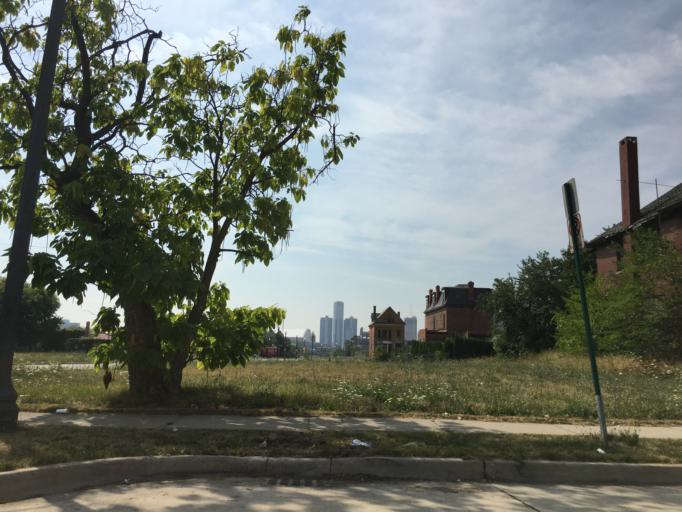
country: US
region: Michigan
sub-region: Wayne County
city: Detroit
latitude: 42.3474
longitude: -83.0526
